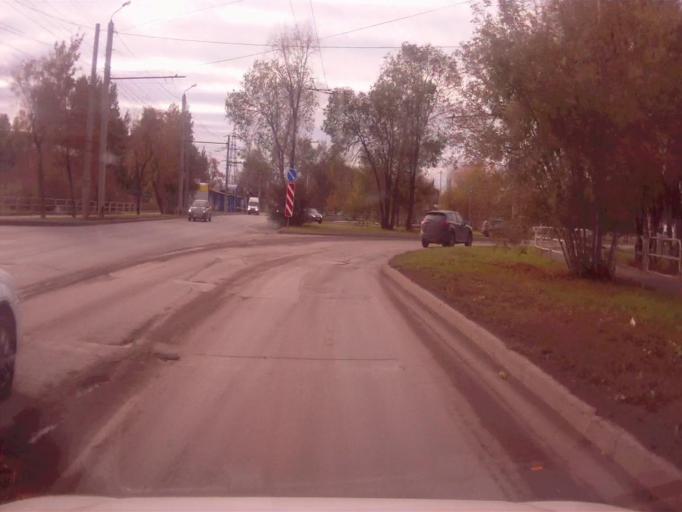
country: RU
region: Chelyabinsk
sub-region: Gorod Chelyabinsk
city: Chelyabinsk
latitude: 55.1160
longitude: 61.4269
